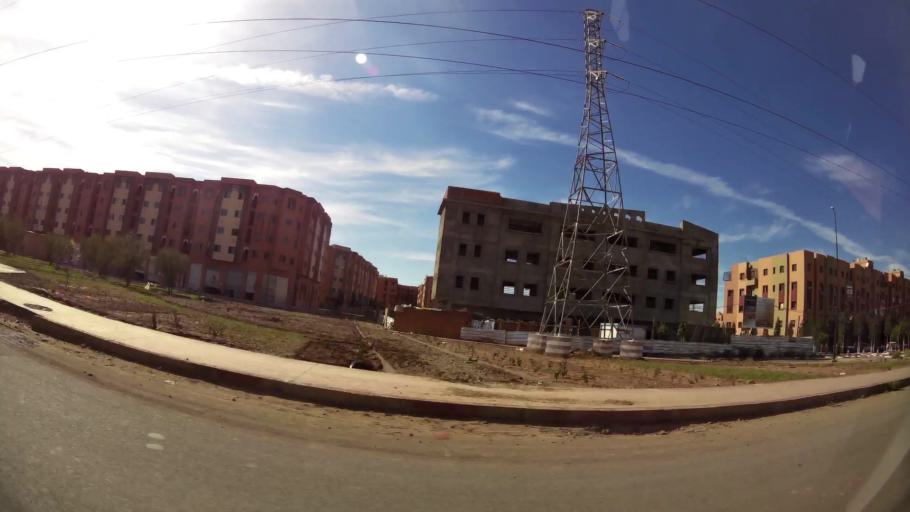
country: MA
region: Marrakech-Tensift-Al Haouz
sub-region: Marrakech
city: Marrakesh
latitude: 31.6495
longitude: -8.0356
